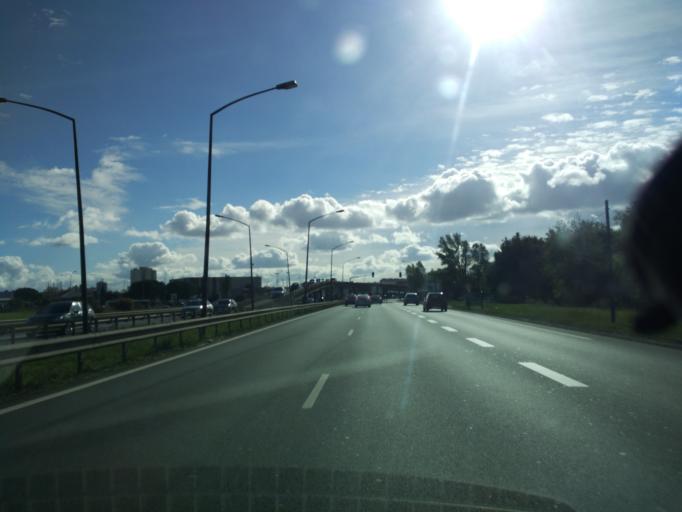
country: FR
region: Aquitaine
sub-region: Departement de la Gironde
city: Le Bouscat
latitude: 44.8720
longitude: -0.5659
